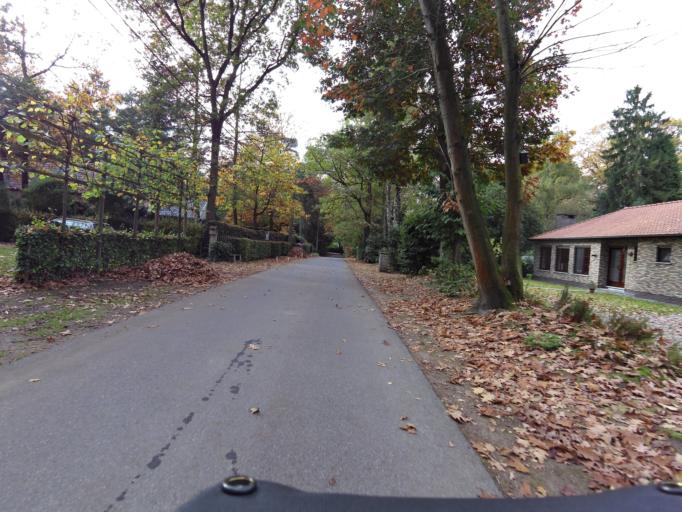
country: BE
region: Flanders
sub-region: Provincie Antwerpen
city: Kalmthout
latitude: 51.3629
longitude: 4.4491
